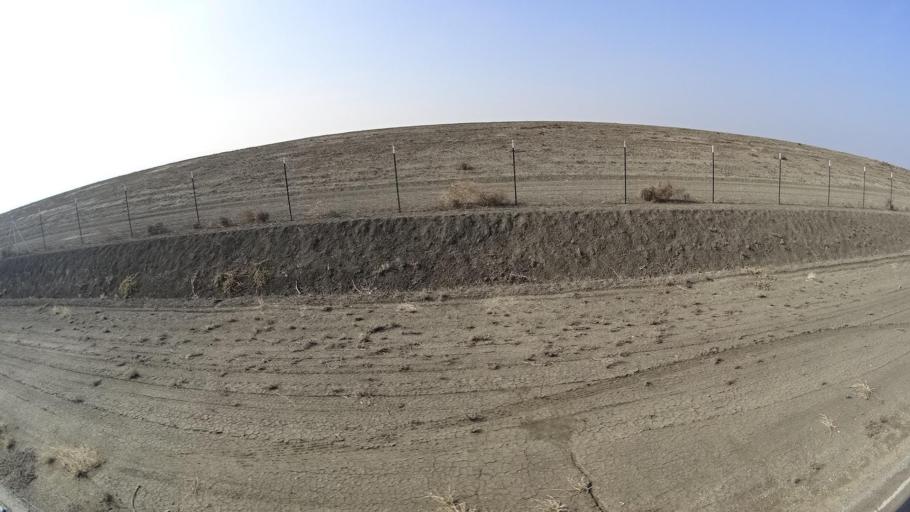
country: US
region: California
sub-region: Kern County
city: Buttonwillow
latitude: 35.3180
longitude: -119.3768
